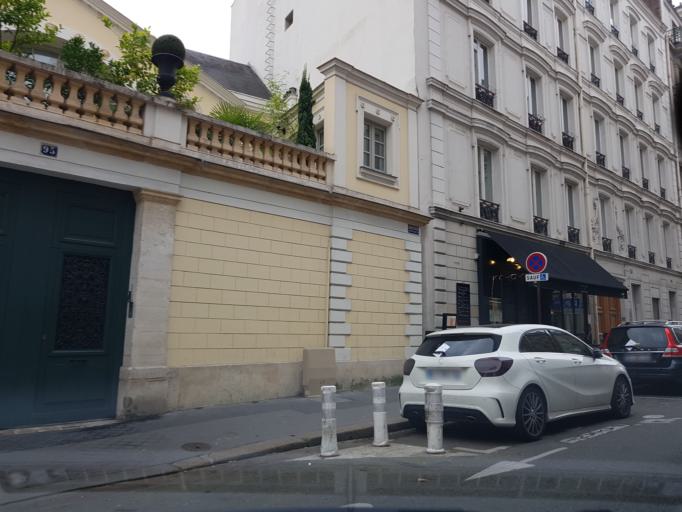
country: FR
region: Ile-de-France
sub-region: Paris
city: Paris
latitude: 48.8469
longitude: 2.3215
